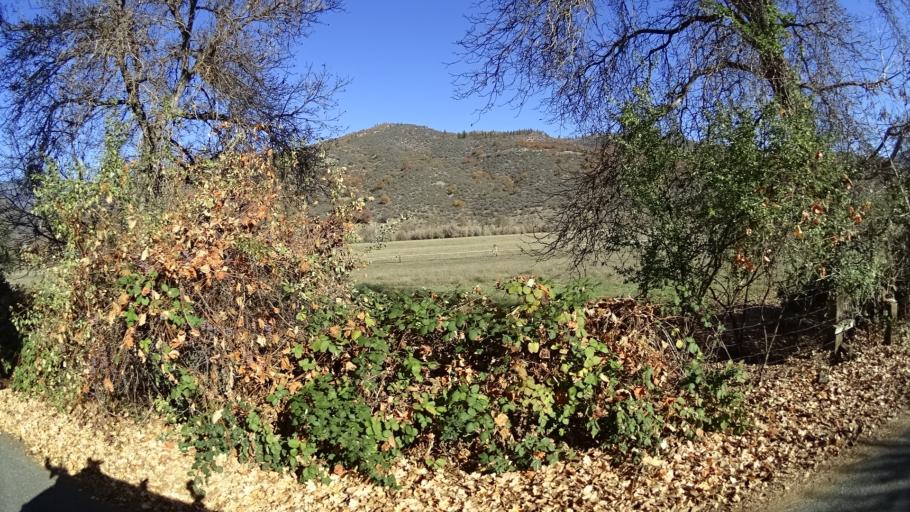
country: US
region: California
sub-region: Siskiyou County
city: Yreka
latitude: 41.8349
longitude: -122.8628
